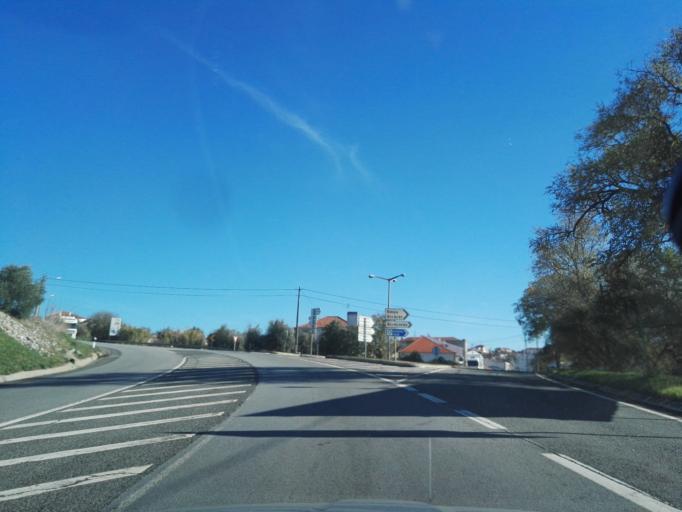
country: PT
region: Evora
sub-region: Montemor-O-Novo
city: Montemor-o-Novo
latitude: 38.6487
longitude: -8.2235
